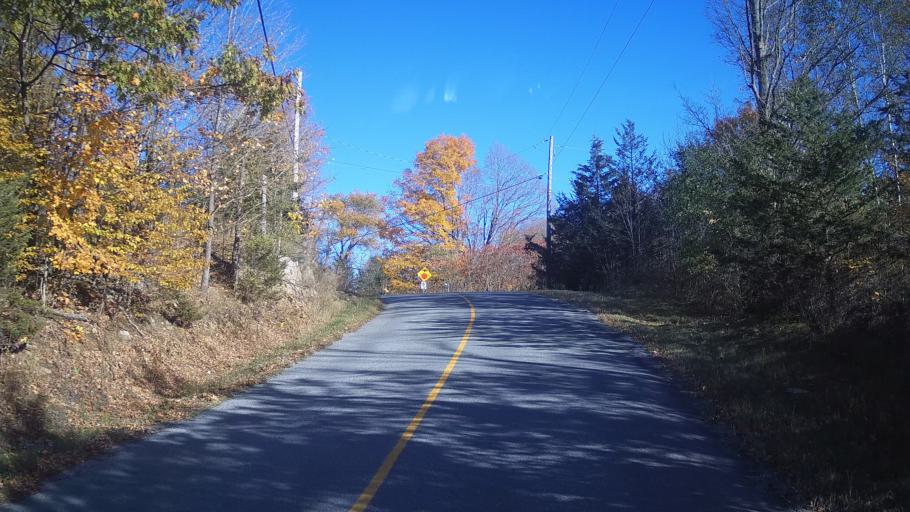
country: CA
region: Ontario
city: Kingston
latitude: 44.4661
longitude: -76.4958
